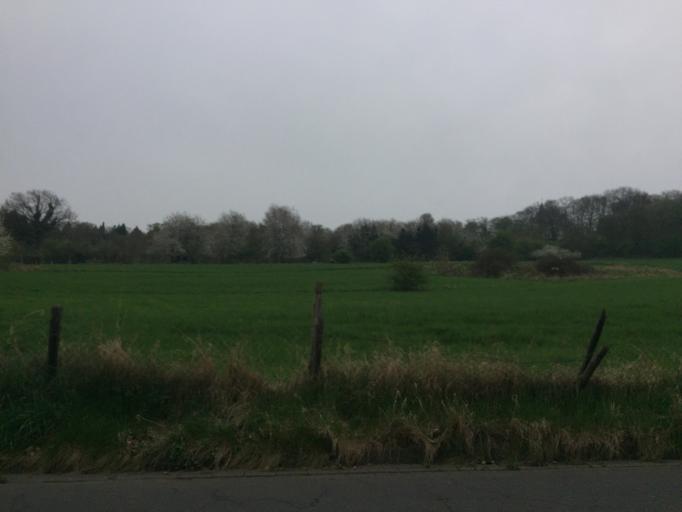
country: DE
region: North Rhine-Westphalia
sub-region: Regierungsbezirk Koln
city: Bonn
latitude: 50.7165
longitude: 7.0766
